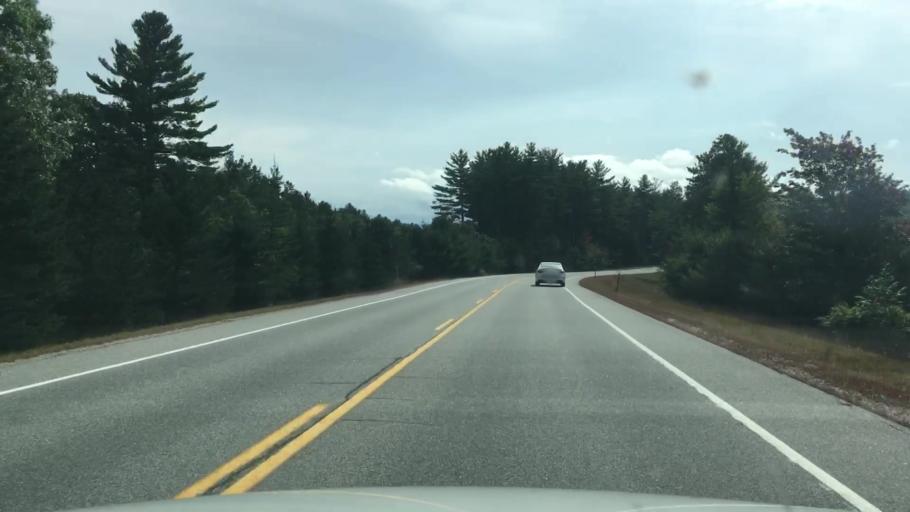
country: US
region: New Hampshire
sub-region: Carroll County
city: North Conway
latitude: 44.0249
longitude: -71.1097
